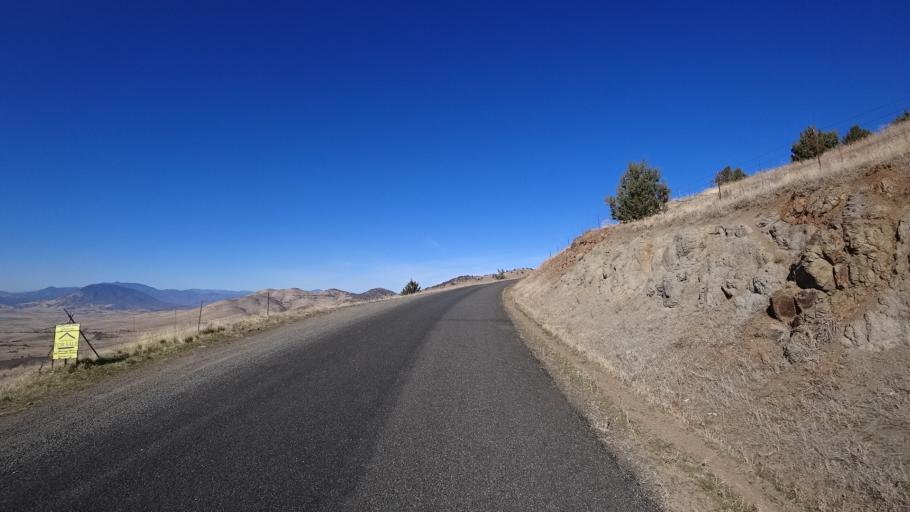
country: US
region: California
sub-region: Siskiyou County
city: Montague
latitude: 41.8253
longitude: -122.3377
